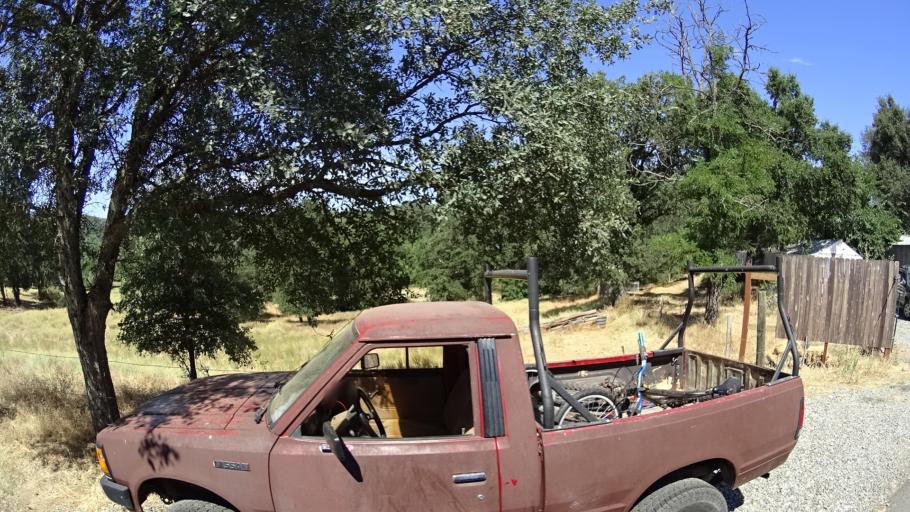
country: US
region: California
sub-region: Calaveras County
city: Angels Camp
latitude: 38.0645
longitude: -120.5383
